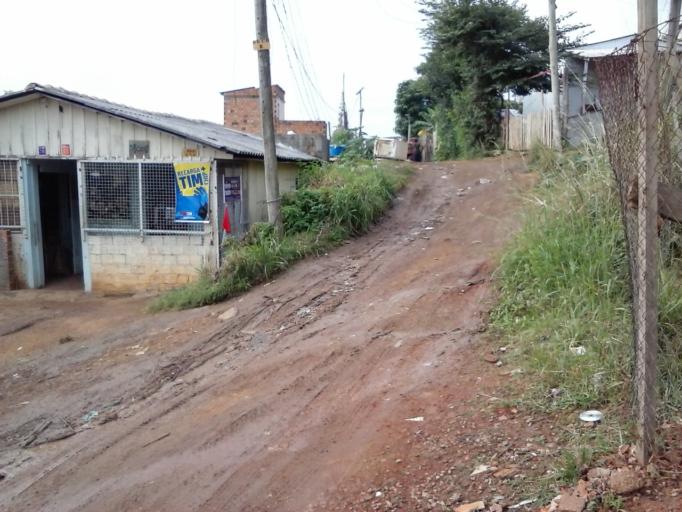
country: BR
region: Rio Grande do Sul
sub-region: Porto Alegre
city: Porto Alegre
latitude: -30.0599
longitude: -51.1417
